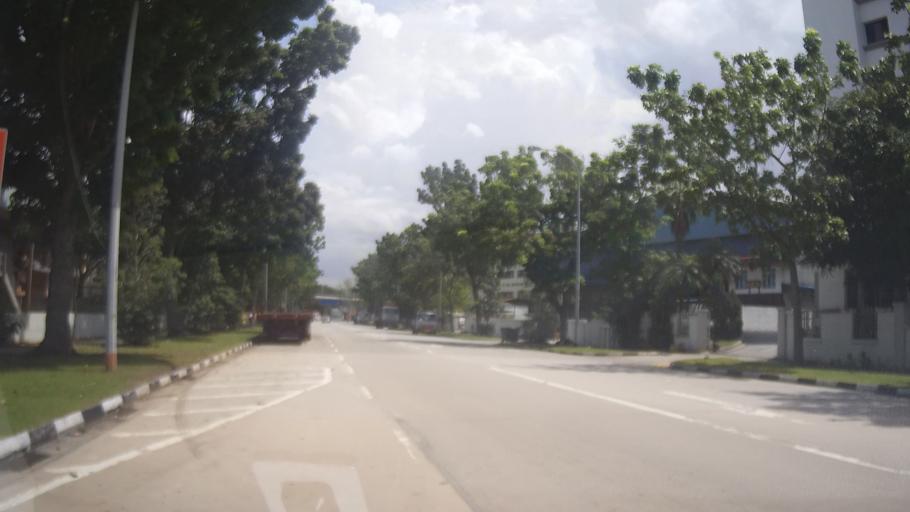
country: MY
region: Johor
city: Johor Bahru
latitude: 1.4061
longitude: 103.7520
